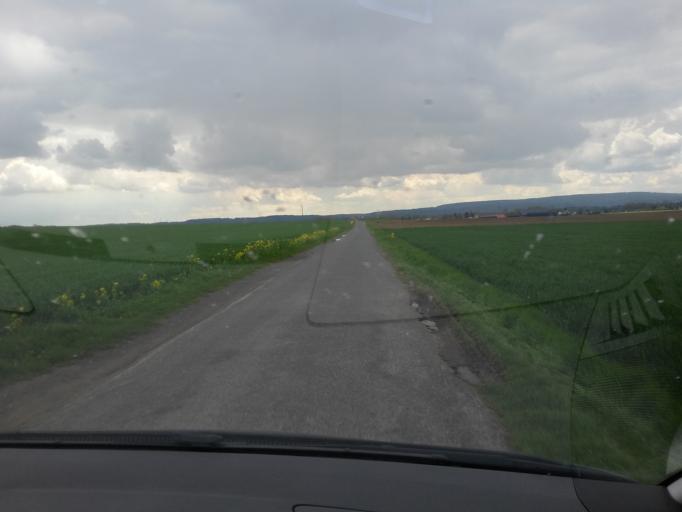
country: FR
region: Picardie
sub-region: Departement de l'Oise
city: Chevrieres
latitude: 49.3625
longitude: 2.6843
